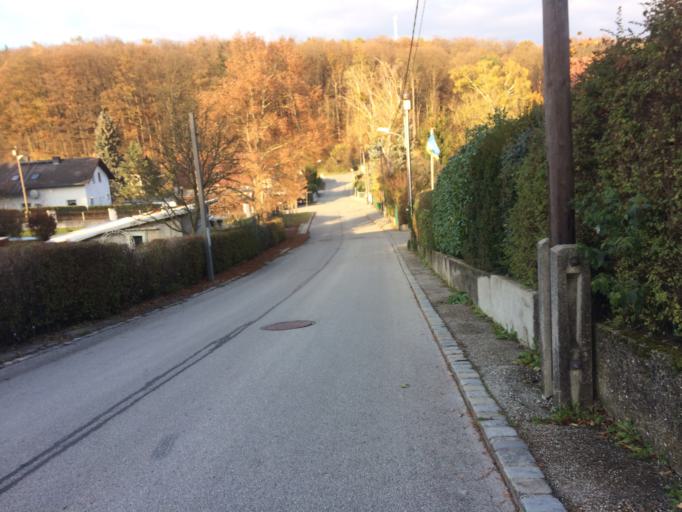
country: AT
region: Lower Austria
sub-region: Politischer Bezirk Wien-Umgebung
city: Gablitz
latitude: 48.2220
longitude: 16.1368
